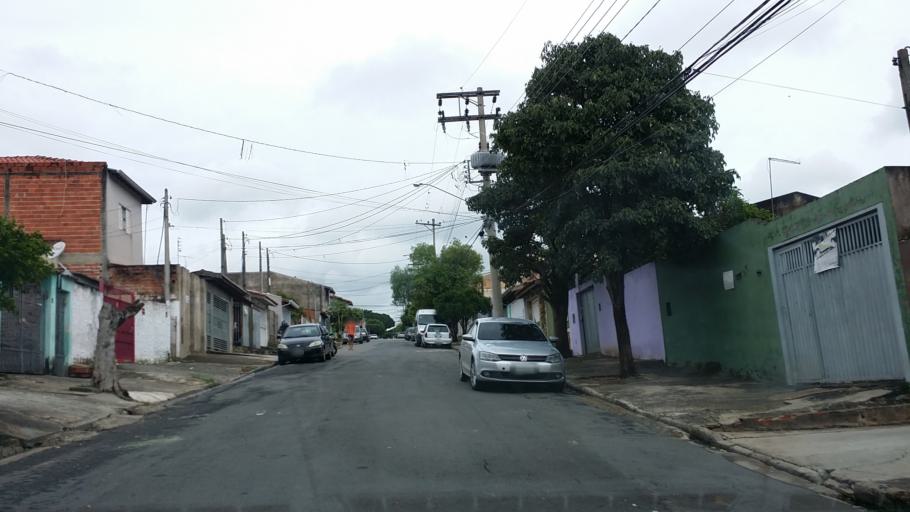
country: BR
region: Sao Paulo
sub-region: Indaiatuba
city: Indaiatuba
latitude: -23.1197
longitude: -47.2305
